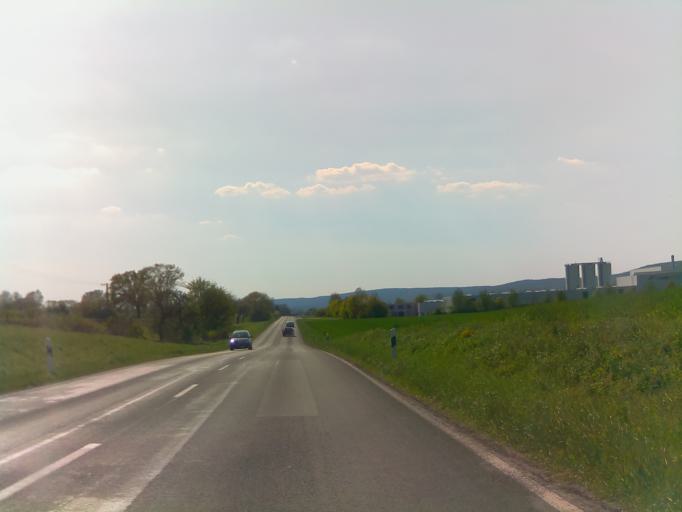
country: DE
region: Thuringia
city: Dreitzsch
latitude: 50.7382
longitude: 11.7878
